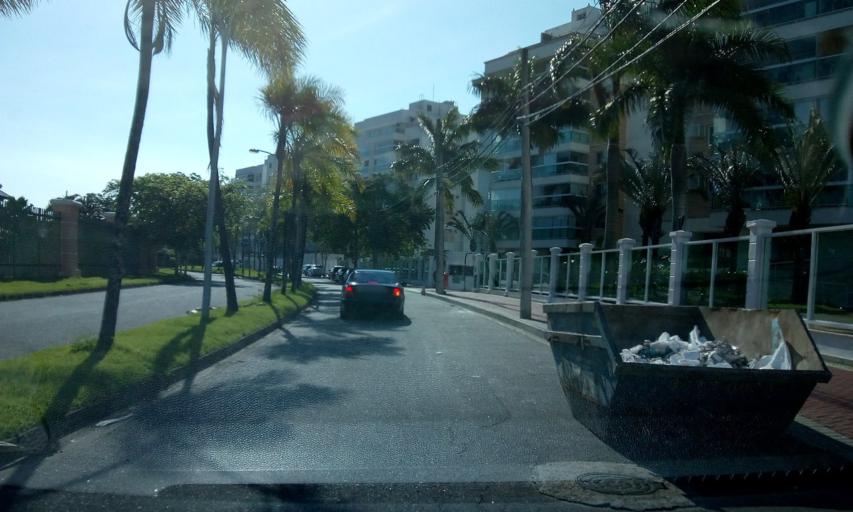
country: BR
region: Rio de Janeiro
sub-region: Nilopolis
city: Nilopolis
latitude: -22.9841
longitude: -43.3816
